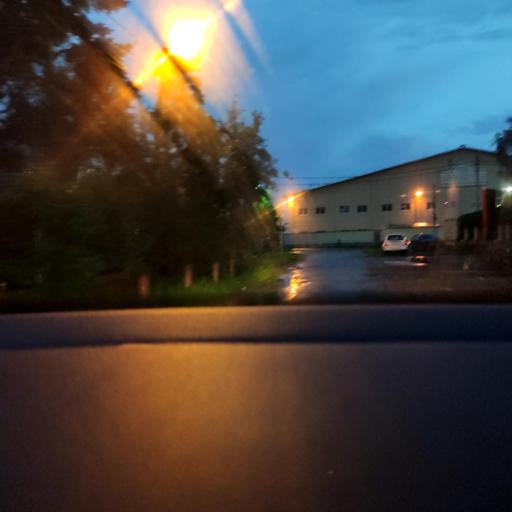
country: RU
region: Moskovskaya
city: Sheremet'yevskiy
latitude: 55.9969
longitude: 37.5445
